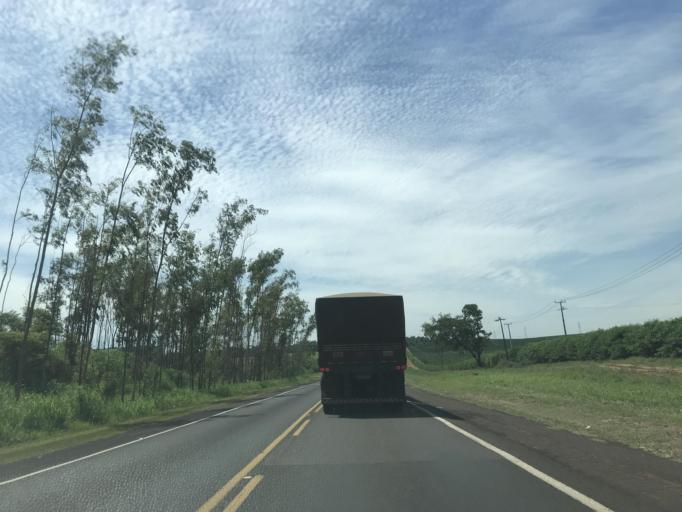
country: BR
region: Parana
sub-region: Paranavai
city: Nova Aurora
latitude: -22.9580
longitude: -52.6545
